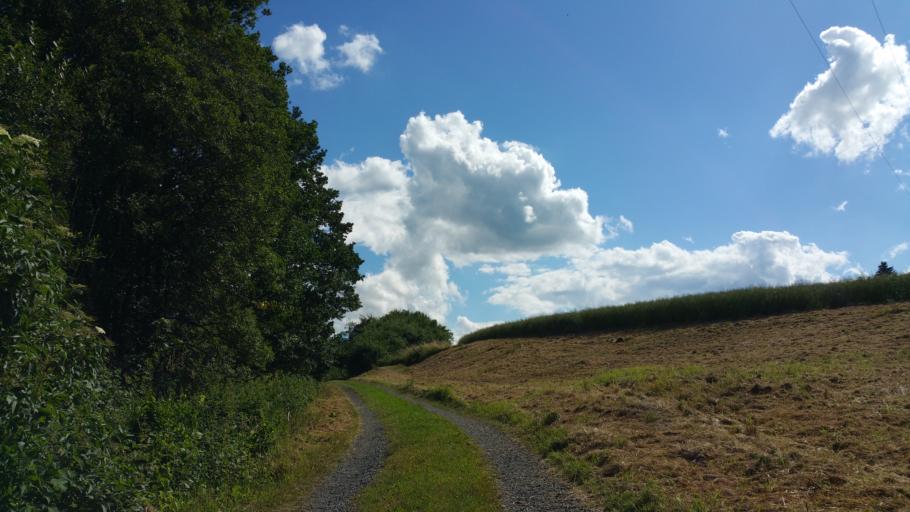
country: DE
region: Bavaria
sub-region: Upper Franconia
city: Schwarzenbach an der Saale
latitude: 50.2157
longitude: 11.9293
